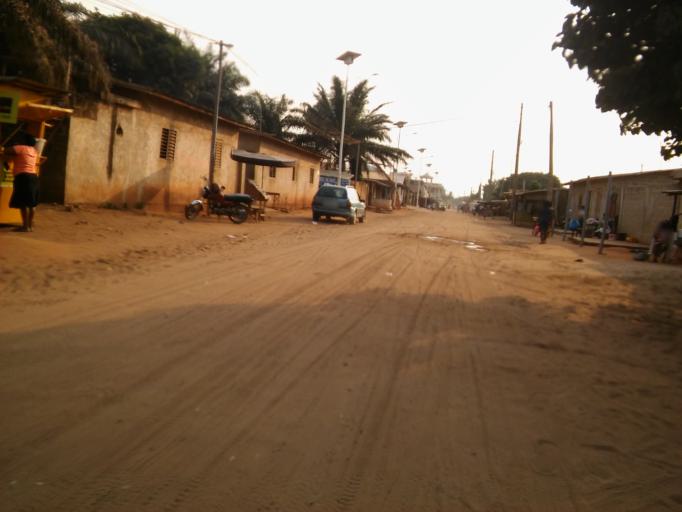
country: BJ
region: Atlantique
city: Abomey-Calavi
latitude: 6.4033
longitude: 2.3288
